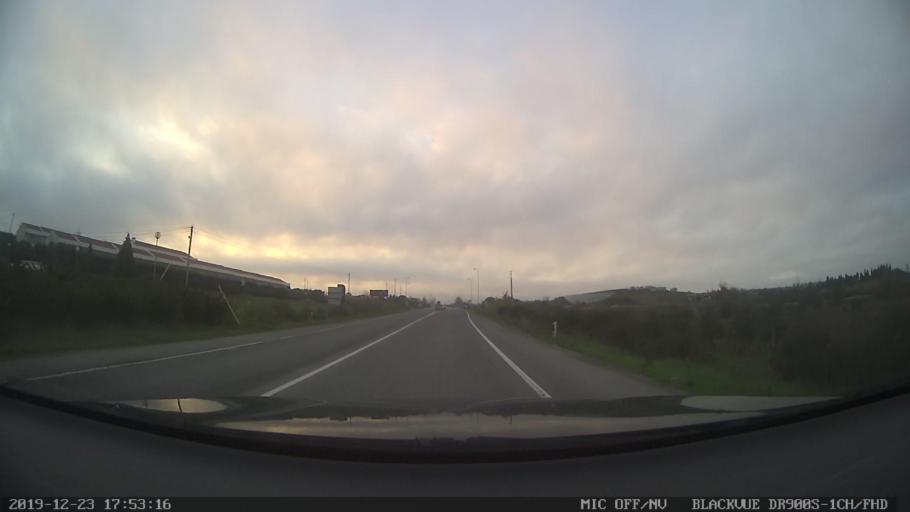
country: PT
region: Aveiro
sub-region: Mealhada
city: Mealhada
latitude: 40.3728
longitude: -8.4806
